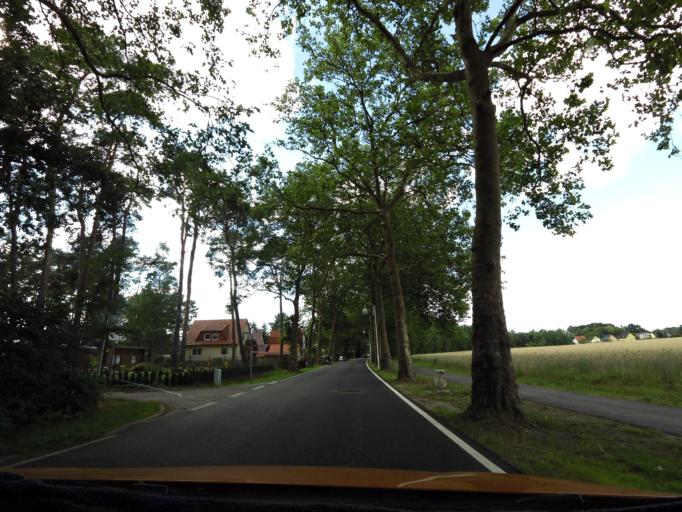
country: DE
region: Brandenburg
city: Rangsdorf
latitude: 52.3453
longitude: 13.4288
